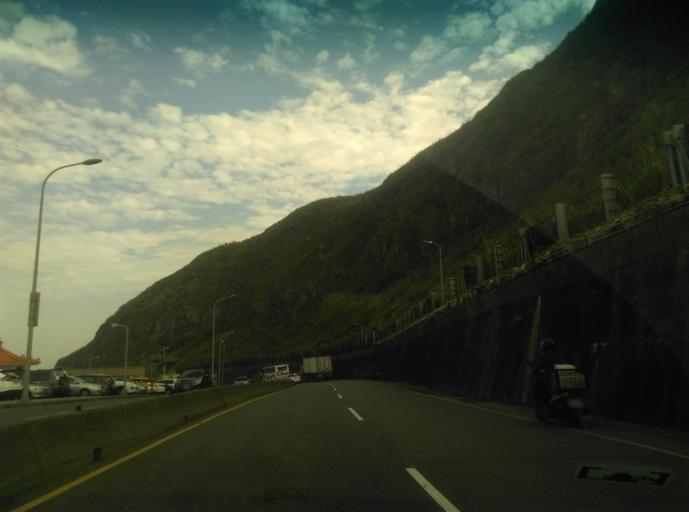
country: TW
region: Taiwan
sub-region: Keelung
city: Keelung
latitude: 25.1753
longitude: 121.7049
